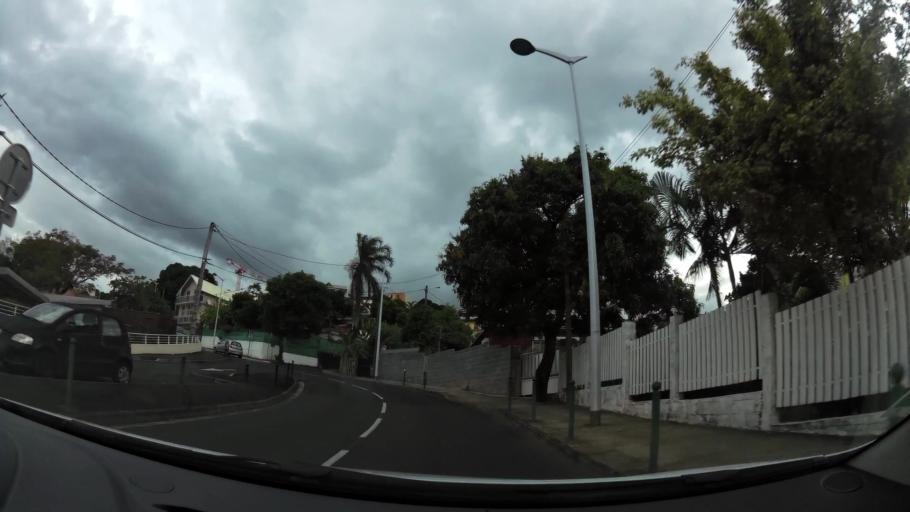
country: RE
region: Reunion
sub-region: Reunion
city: Saint-Denis
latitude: -20.8963
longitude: 55.4670
